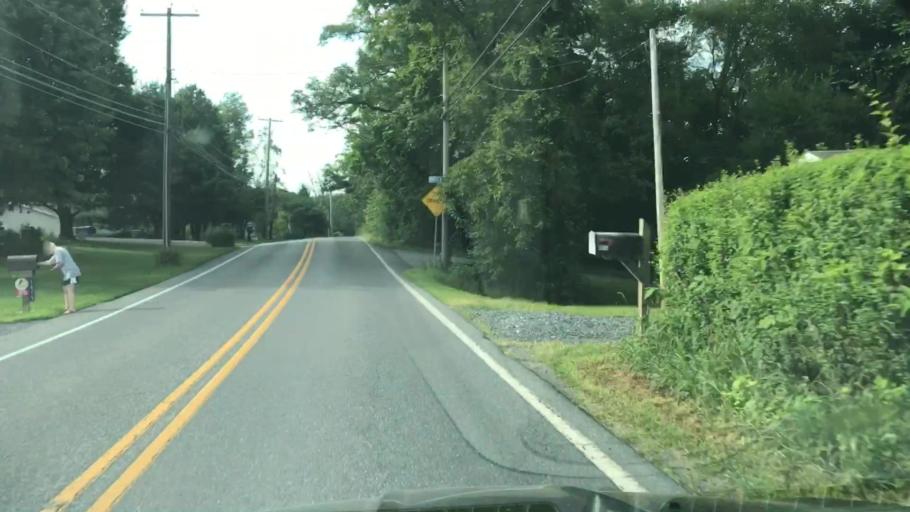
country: US
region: Pennsylvania
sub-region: Dauphin County
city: Middletown
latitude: 40.2210
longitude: -76.7359
